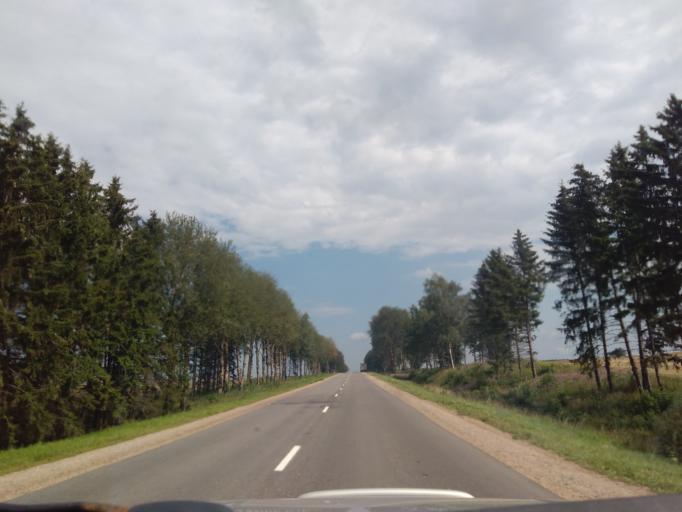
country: BY
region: Minsk
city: Khatsyezhyna
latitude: 53.9121
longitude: 27.3347
